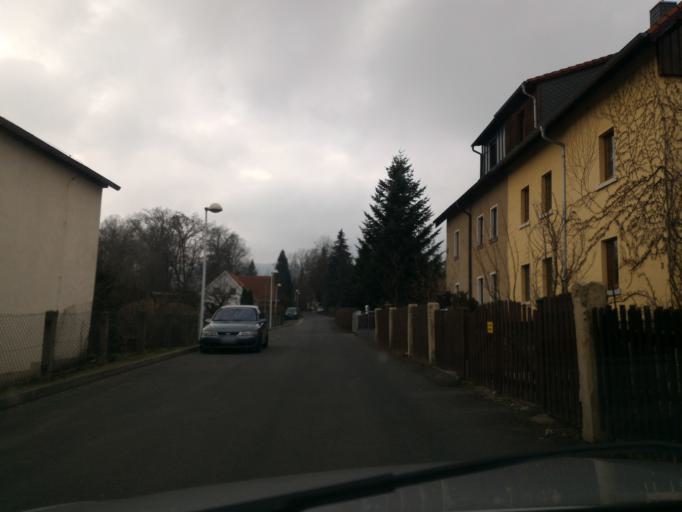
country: DE
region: Saxony
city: Olbersdorf
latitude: 50.8595
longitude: 14.7935
